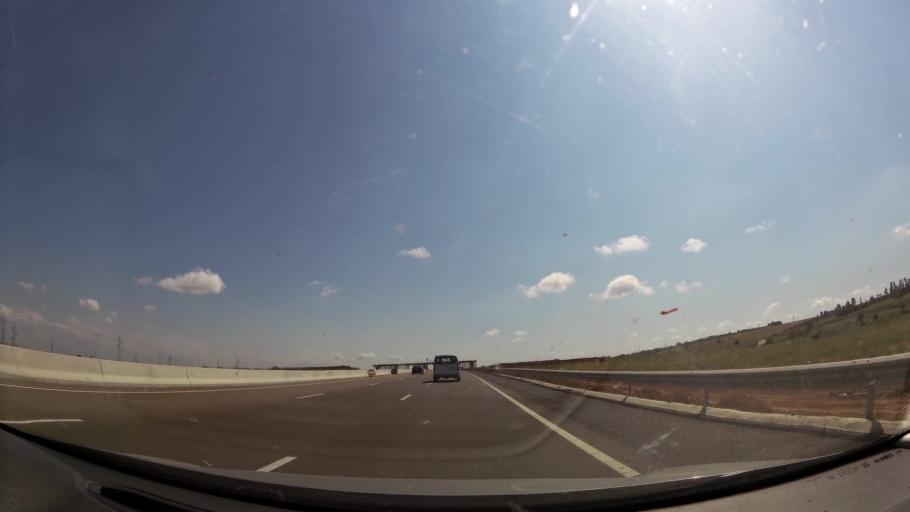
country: MA
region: Rabat-Sale-Zemmour-Zaer
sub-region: Rabat
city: Rabat
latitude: 33.9202
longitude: -6.7689
